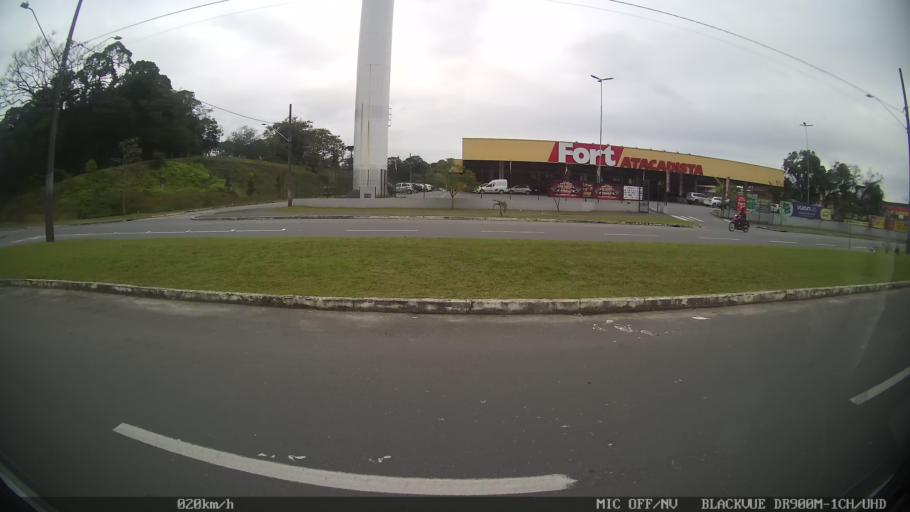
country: BR
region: Santa Catarina
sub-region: Joinville
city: Joinville
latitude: -26.2738
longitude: -48.8772
